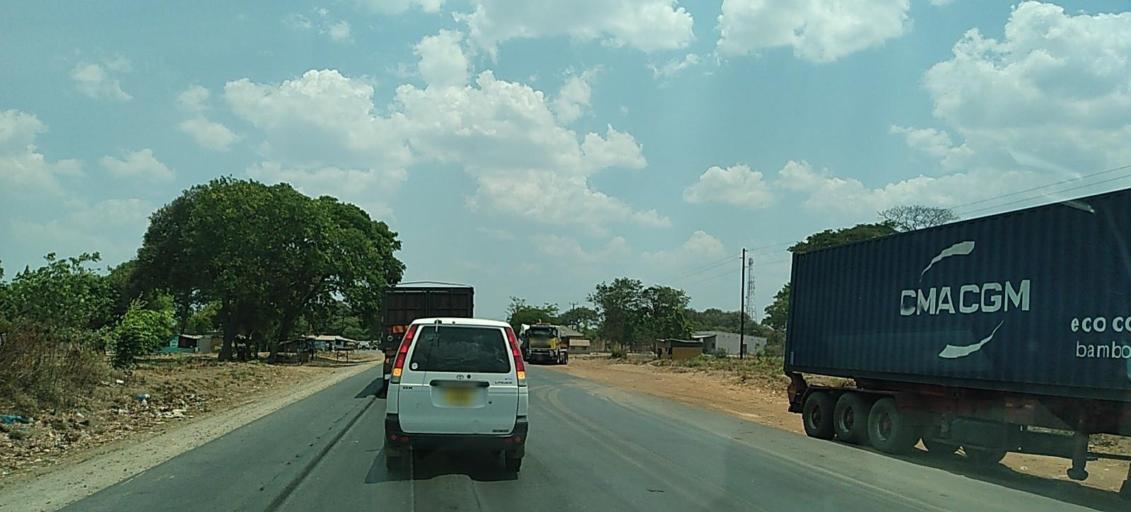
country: ZM
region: Central
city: Kabwe
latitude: -14.2205
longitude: 28.5769
